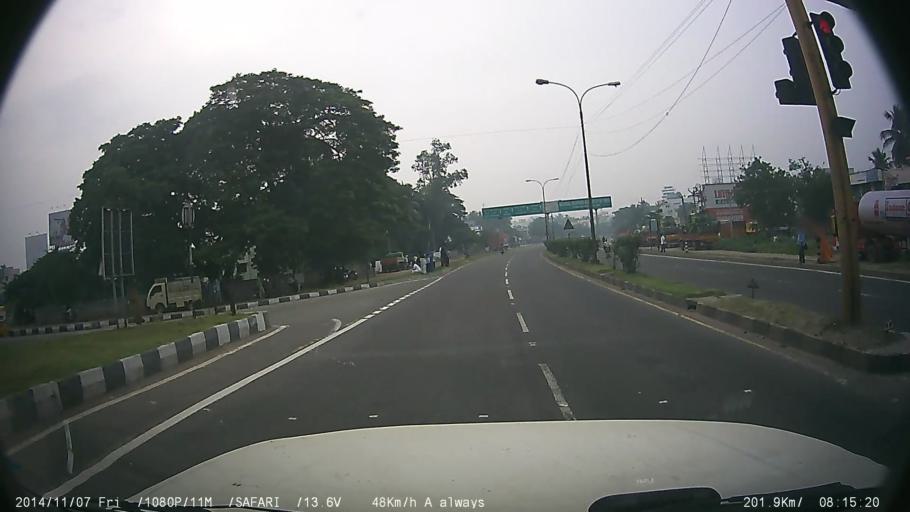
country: IN
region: Tamil Nadu
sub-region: Salem
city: Salem
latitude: 11.6818
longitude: 78.1266
